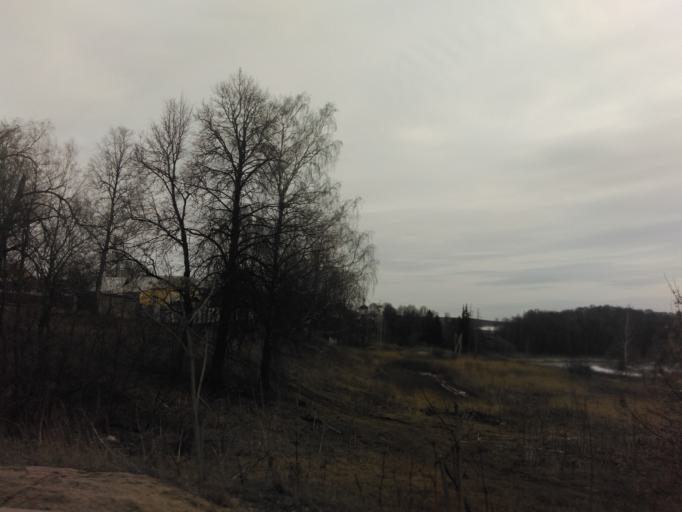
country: RU
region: Moskovskaya
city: Tuchkovo
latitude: 55.6190
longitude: 36.5069
